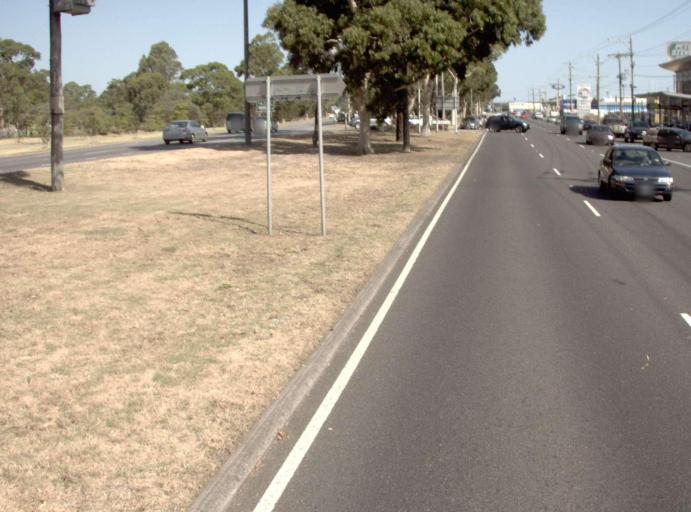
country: AU
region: Victoria
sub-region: Greater Dandenong
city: Dandenong
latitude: -37.9941
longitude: 145.2167
